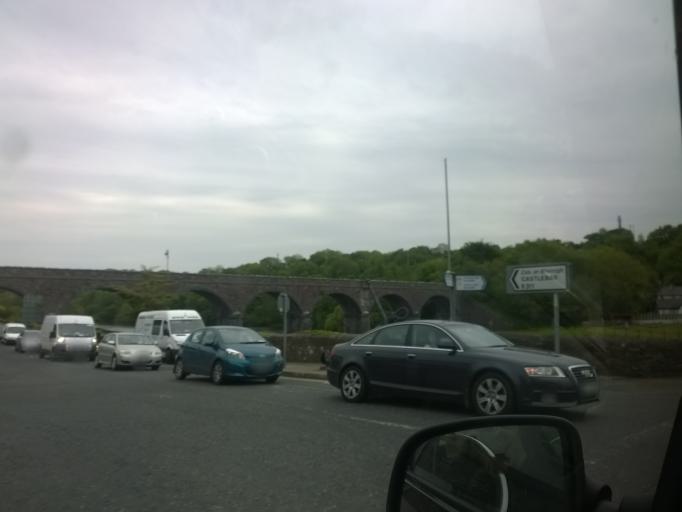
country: IE
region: Connaught
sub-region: Maigh Eo
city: Westport
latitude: 53.8845
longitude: -9.5461
